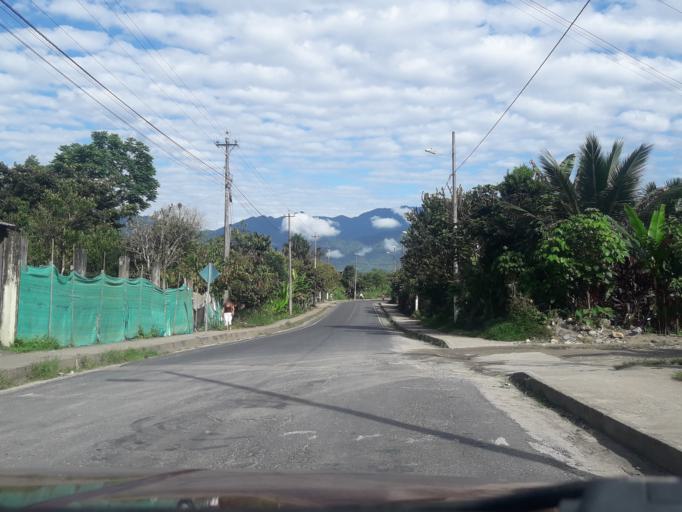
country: EC
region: Napo
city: Tena
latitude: -0.9846
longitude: -77.8391
